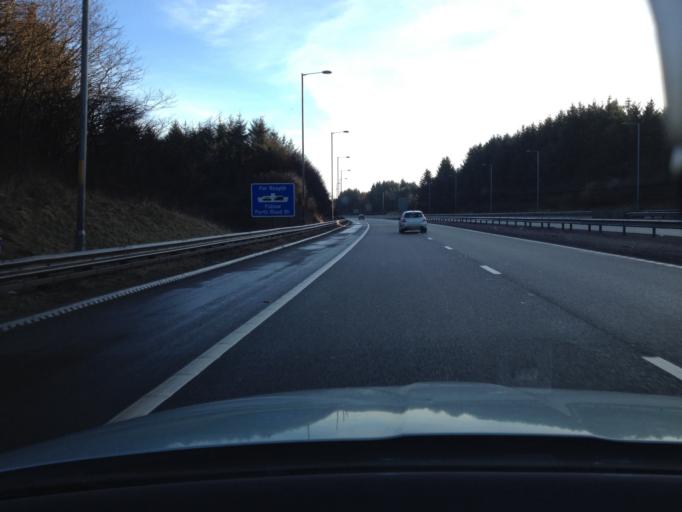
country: GB
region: Scotland
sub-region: West Lothian
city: Livingston
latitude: 55.9165
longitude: -3.5206
